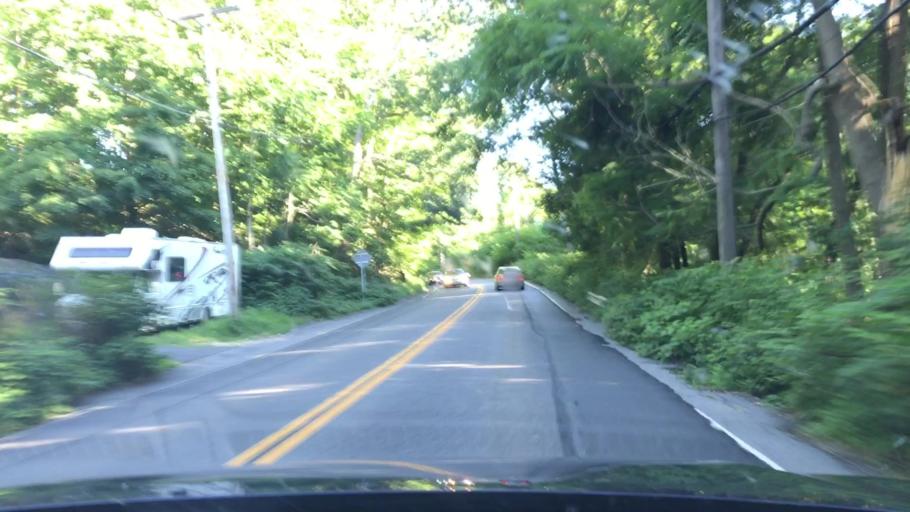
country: US
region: New York
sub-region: Westchester County
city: Heritage Hills
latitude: 41.3444
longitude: -73.6606
